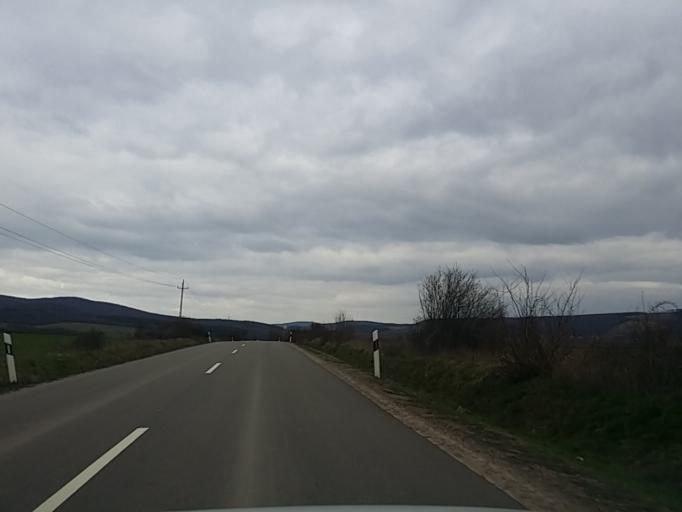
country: HU
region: Heves
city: Verpelet
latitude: 47.8608
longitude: 20.2043
